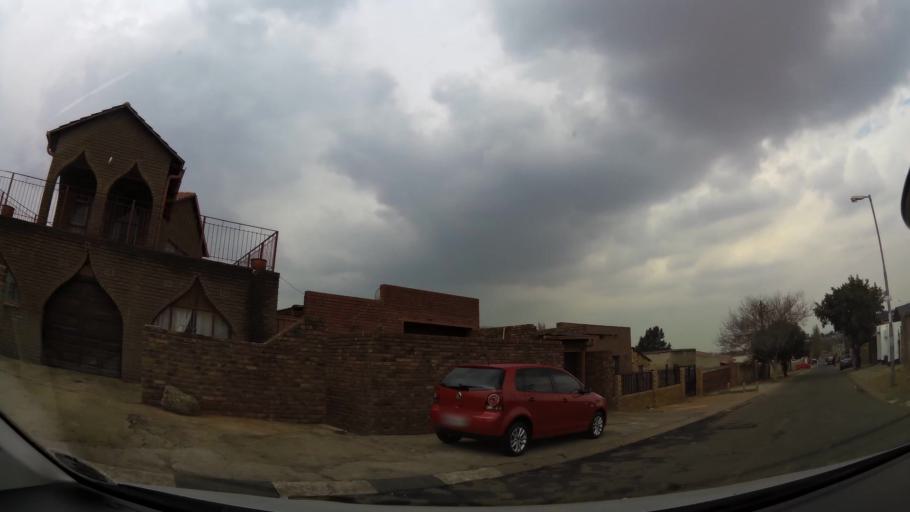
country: ZA
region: Gauteng
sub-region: City of Johannesburg Metropolitan Municipality
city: Soweto
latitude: -26.2617
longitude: 27.8649
